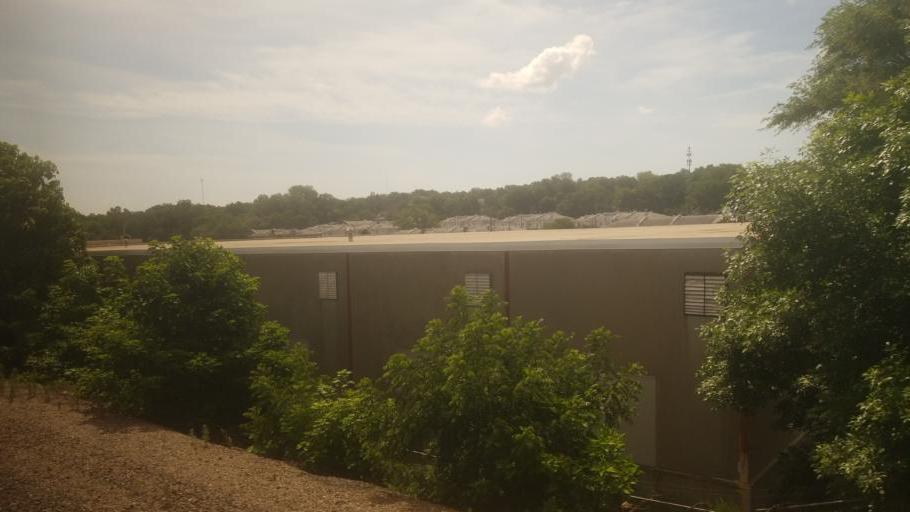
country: US
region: Missouri
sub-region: Clay County
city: North Kansas City
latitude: 39.0997
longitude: -94.5233
